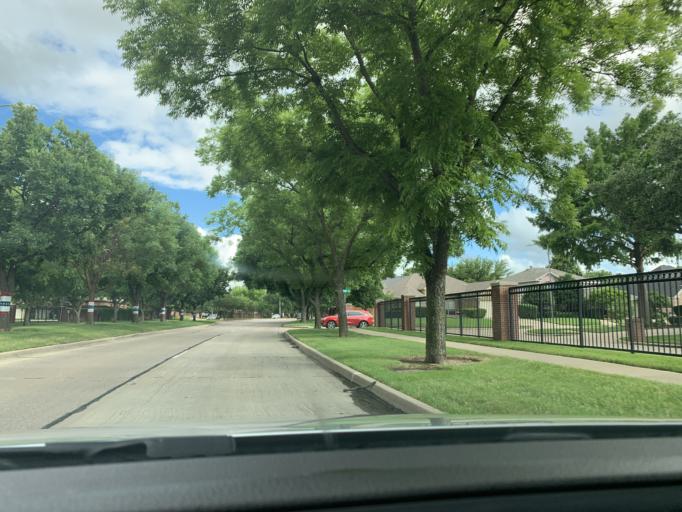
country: US
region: Texas
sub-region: Dallas County
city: Grand Prairie
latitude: 32.6681
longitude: -97.0030
